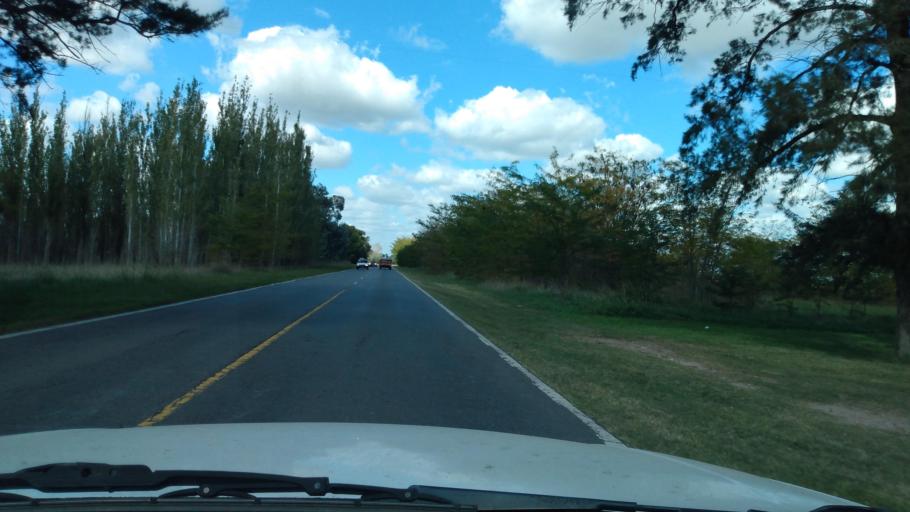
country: AR
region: Buenos Aires
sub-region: Partido de Navarro
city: Navarro
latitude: -34.9350
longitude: -59.3230
